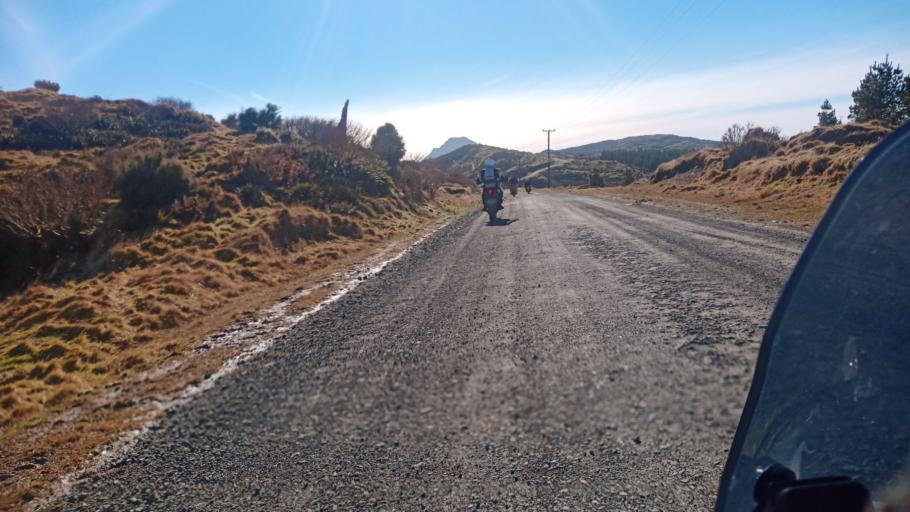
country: NZ
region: Gisborne
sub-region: Gisborne District
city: Gisborne
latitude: -38.1855
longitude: 177.8205
